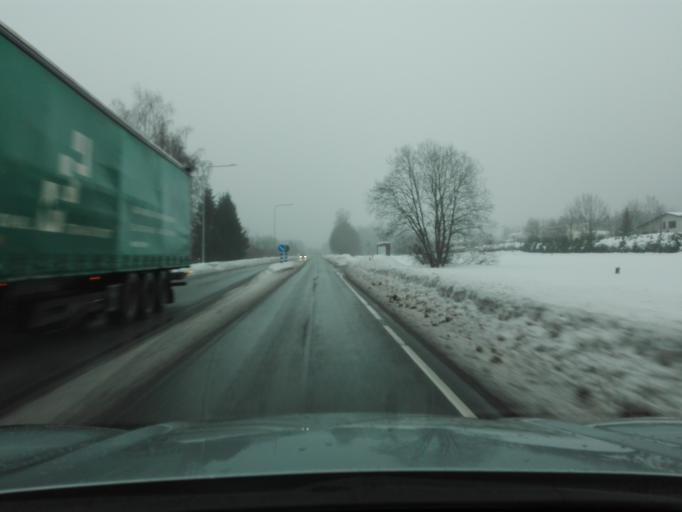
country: EE
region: Harju
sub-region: Kiili vald
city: Kiili
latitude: 59.3399
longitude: 24.7739
